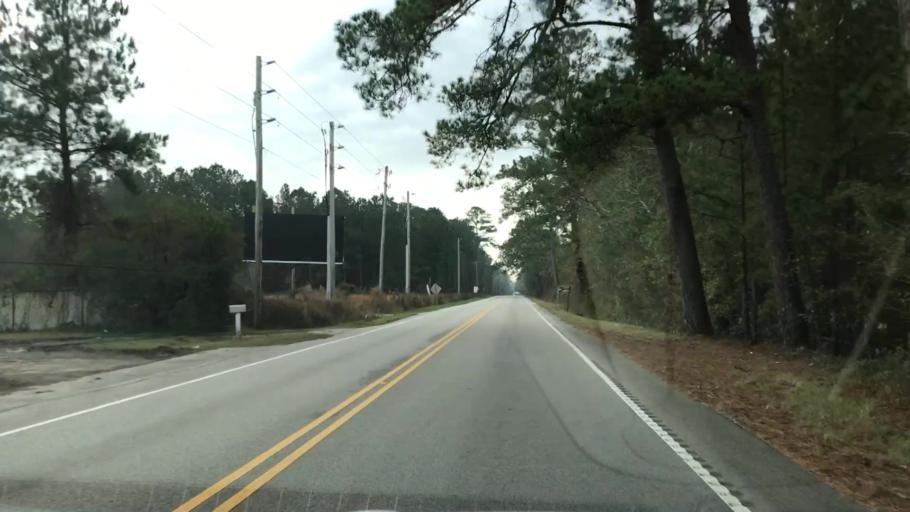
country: US
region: South Carolina
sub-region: Jasper County
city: Ridgeland
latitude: 32.5165
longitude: -80.8898
